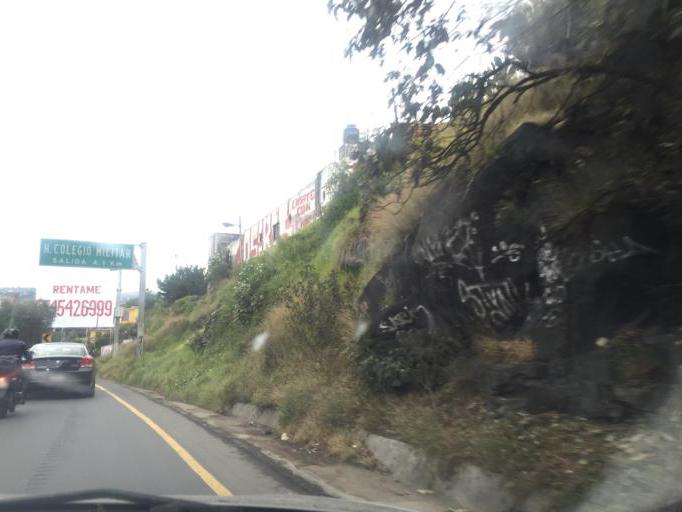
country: MX
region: Mexico City
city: Tlalpan
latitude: 19.2632
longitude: -99.1662
